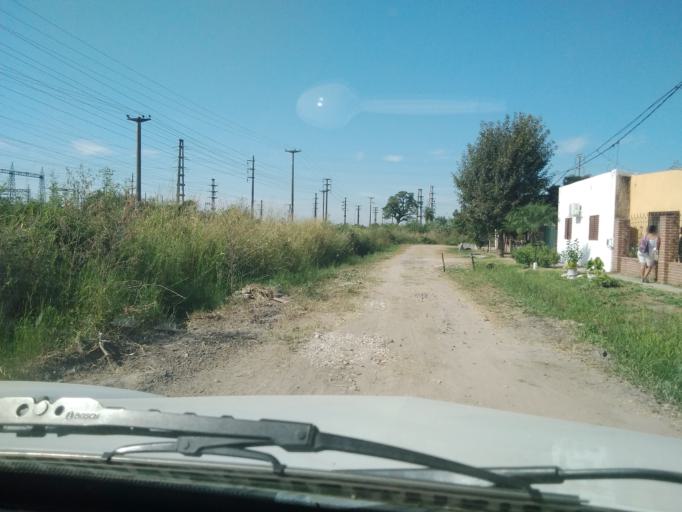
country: AR
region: Corrientes
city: Corrientes
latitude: -27.5123
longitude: -58.7991
